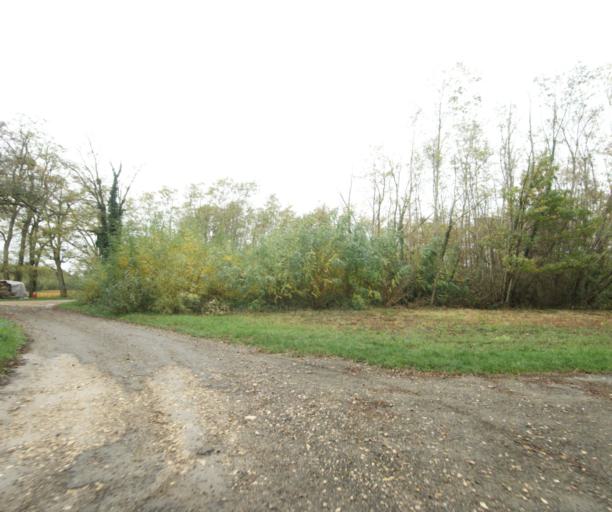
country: FR
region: Bourgogne
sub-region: Departement de Saone-et-Loire
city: Tournus
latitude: 46.4886
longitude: 4.8449
